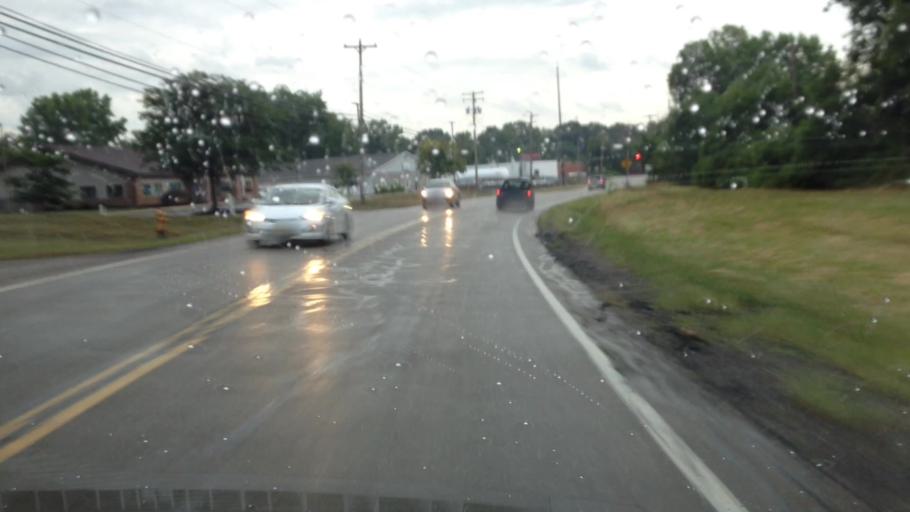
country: US
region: Ohio
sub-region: Summit County
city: Portage Lakes
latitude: 41.0201
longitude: -81.5296
